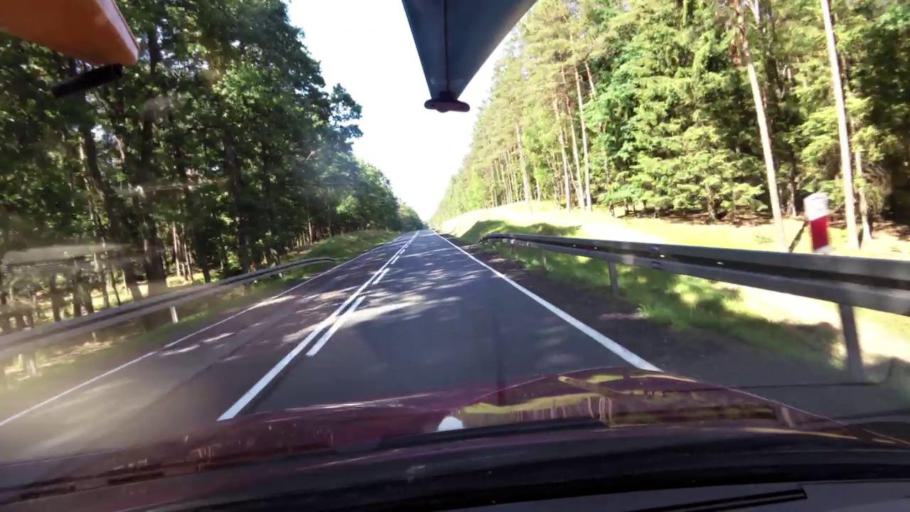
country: PL
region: Pomeranian Voivodeship
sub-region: Powiat bytowski
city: Miastko
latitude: 54.1169
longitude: 17.0007
